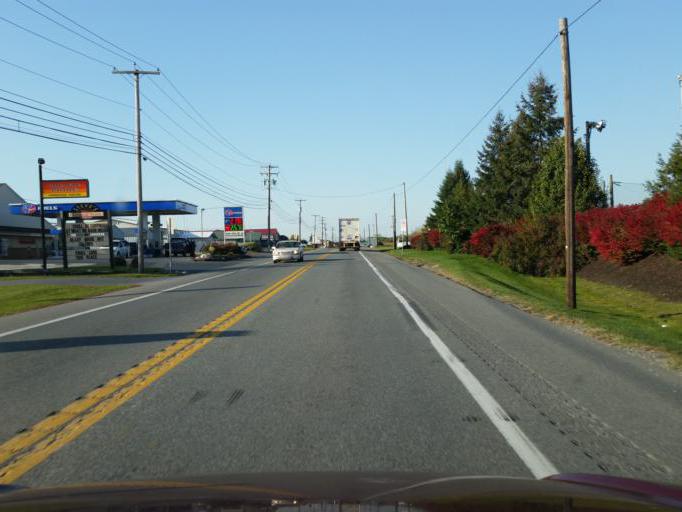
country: US
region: Pennsylvania
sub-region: Lebanon County
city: Campbelltown
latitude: 40.2320
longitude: -76.6222
